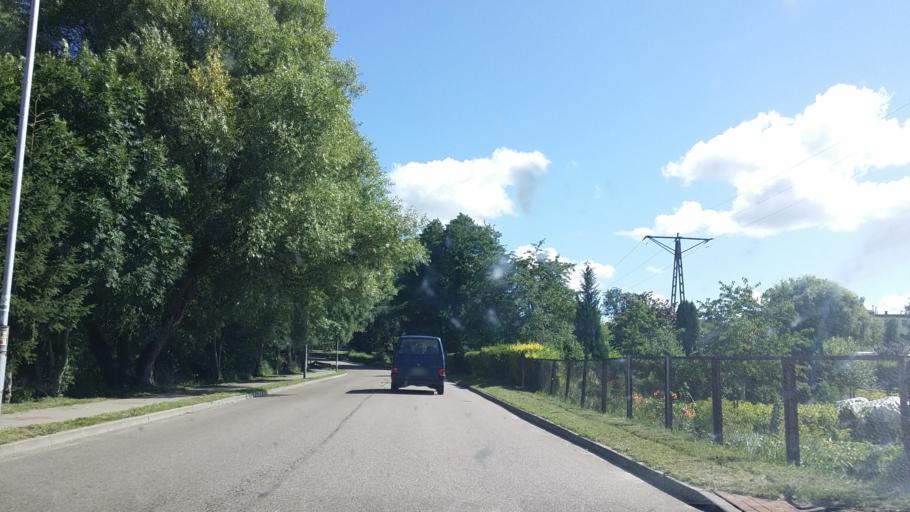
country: PL
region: West Pomeranian Voivodeship
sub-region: Powiat drawski
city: Kalisz Pomorski
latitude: 53.2999
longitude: 15.9071
